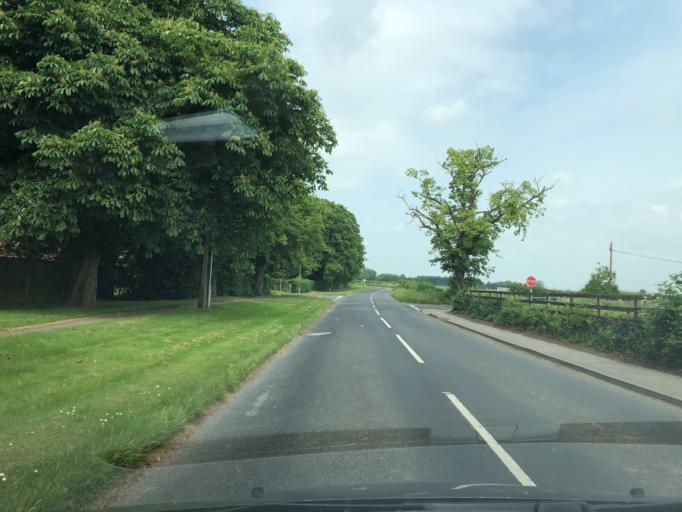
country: GB
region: England
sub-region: North Yorkshire
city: Boroughbridge
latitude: 54.1330
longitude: -1.4058
